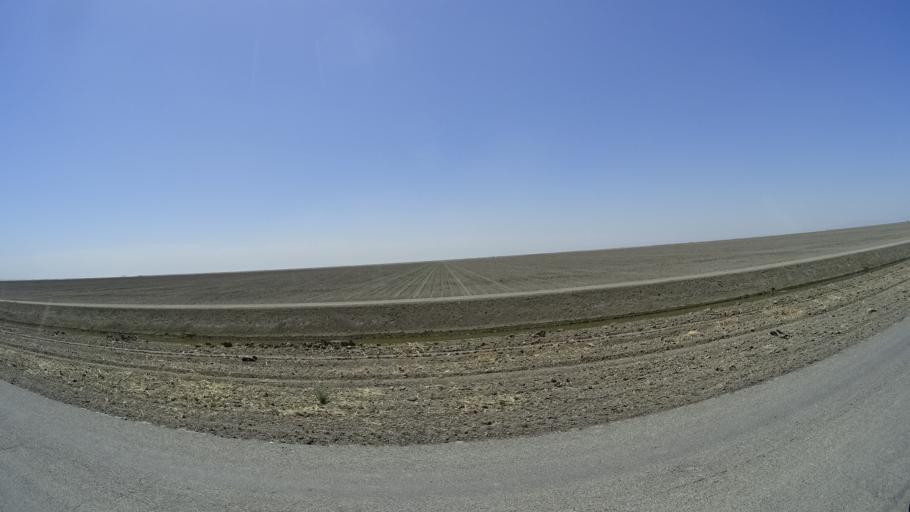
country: US
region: California
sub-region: Kings County
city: Corcoran
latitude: 36.0215
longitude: -119.6050
